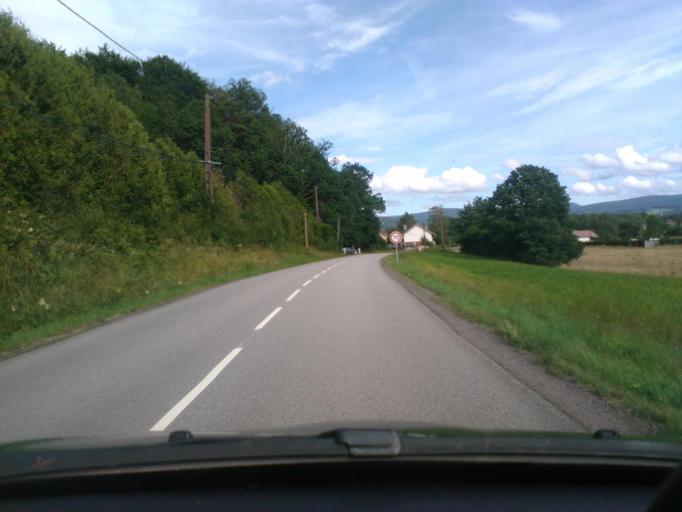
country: FR
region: Lorraine
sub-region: Departement des Vosges
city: Corcieux
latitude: 48.2015
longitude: 6.8498
